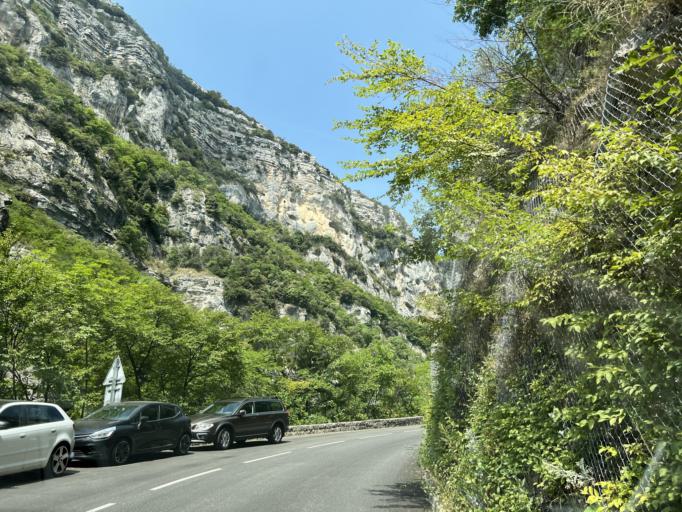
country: FR
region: Provence-Alpes-Cote d'Azur
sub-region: Departement des Alpes-Maritimes
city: Tourrettes-sur-Loup
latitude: 43.7353
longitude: 6.9989
